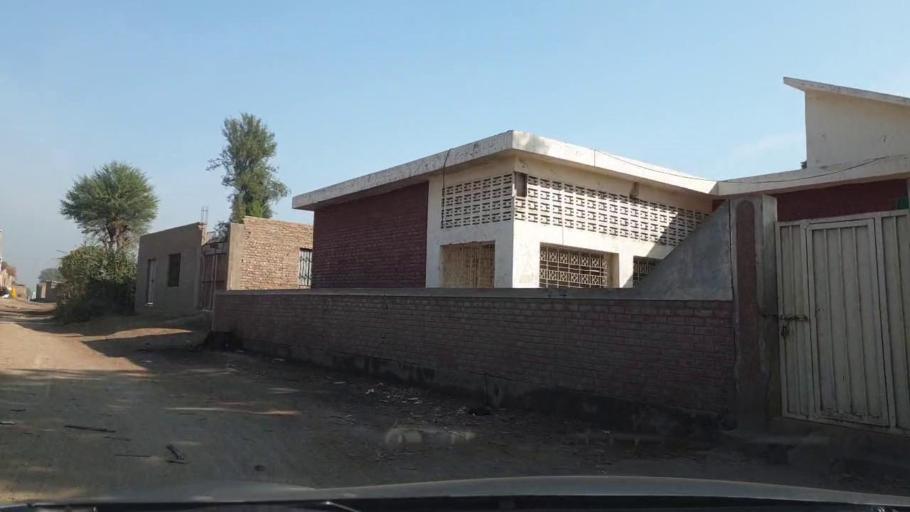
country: PK
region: Sindh
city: Tando Allahyar
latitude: 25.5921
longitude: 68.7232
